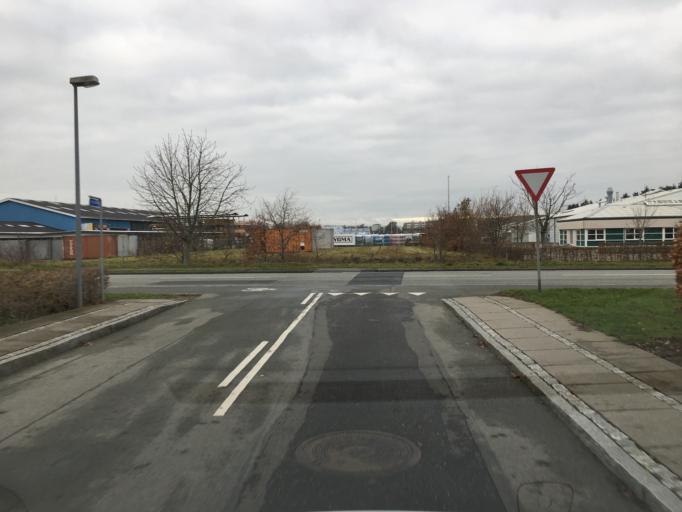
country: DK
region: South Denmark
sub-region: Tonder Kommune
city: Tonder
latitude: 54.9468
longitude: 8.8675
